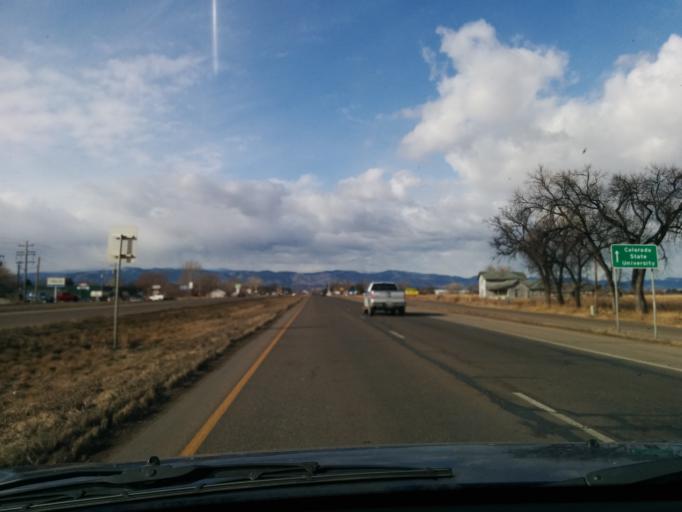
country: US
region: Colorado
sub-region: Larimer County
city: Fort Collins
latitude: 40.5812
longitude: -105.0093
